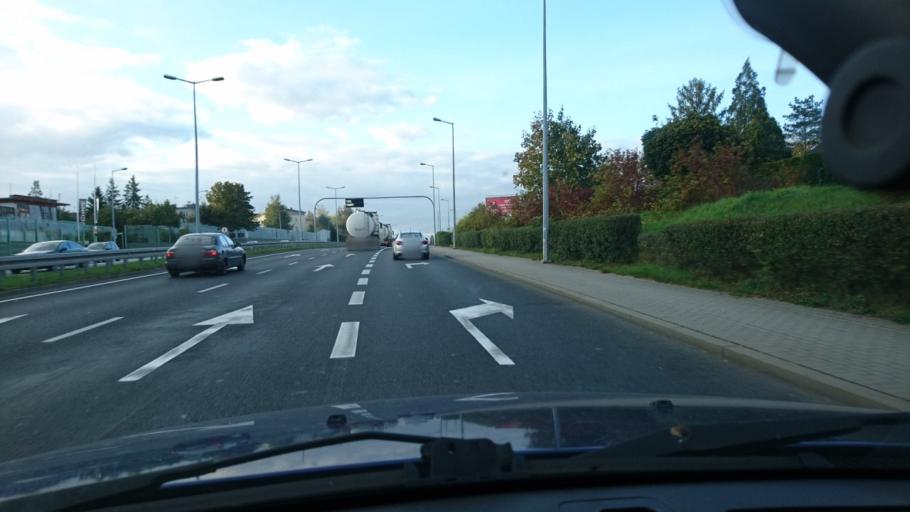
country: PL
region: Silesian Voivodeship
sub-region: Bielsko-Biala
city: Bielsko-Biala
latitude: 49.8127
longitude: 19.0244
